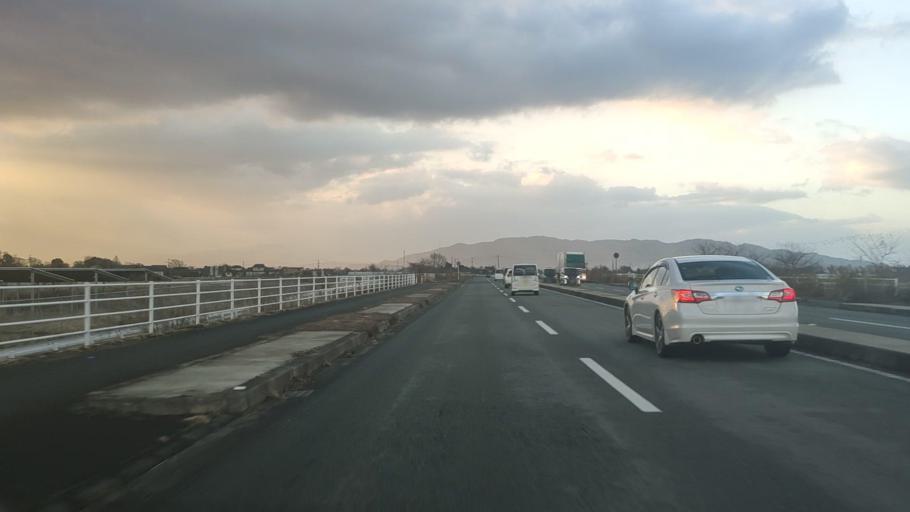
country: JP
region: Kumamoto
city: Kumamoto
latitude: 32.7512
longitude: 130.7067
